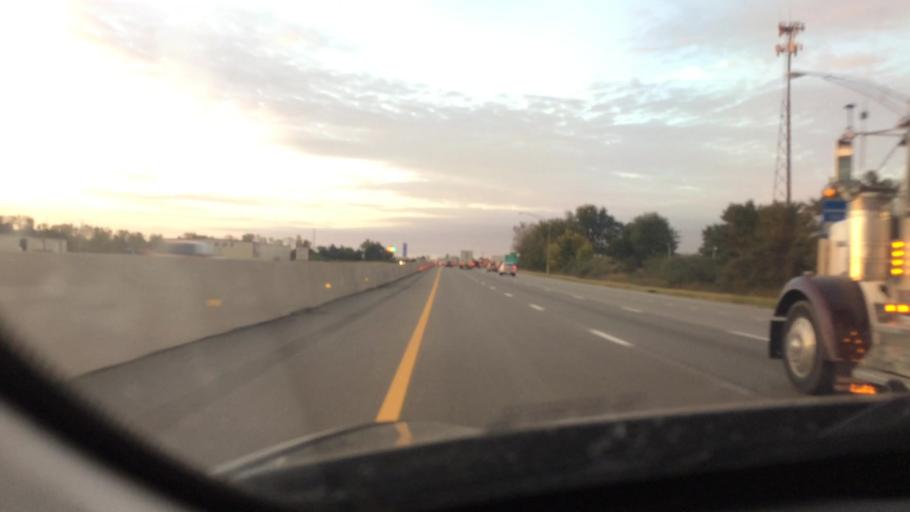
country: US
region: Ohio
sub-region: Hancock County
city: Findlay
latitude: 41.0974
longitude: -83.6600
